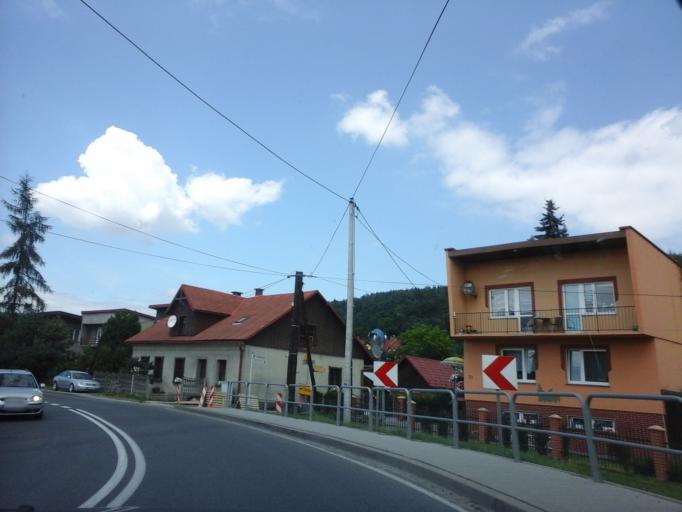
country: PL
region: Lesser Poland Voivodeship
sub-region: Powiat suski
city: Makow Podhalanski
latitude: 49.7258
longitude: 19.6907
